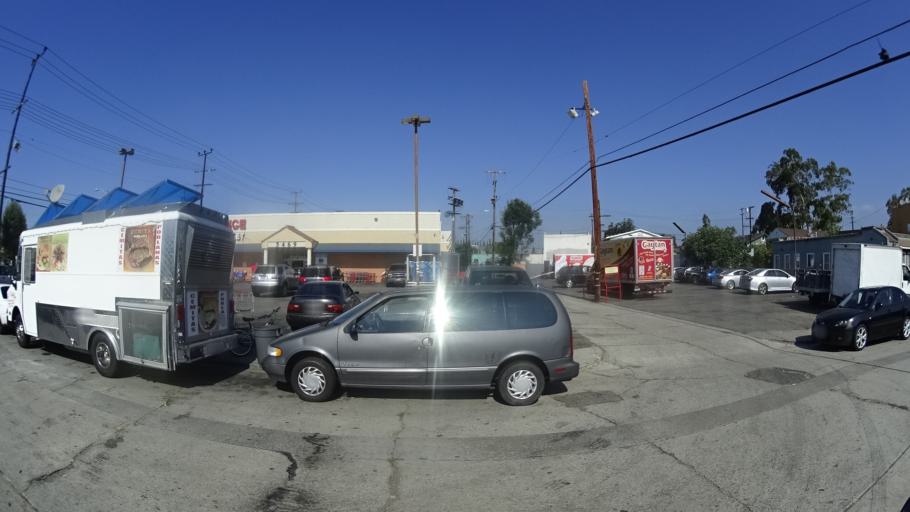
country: US
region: California
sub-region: Los Angeles County
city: Culver City
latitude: 34.0328
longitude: -118.3614
